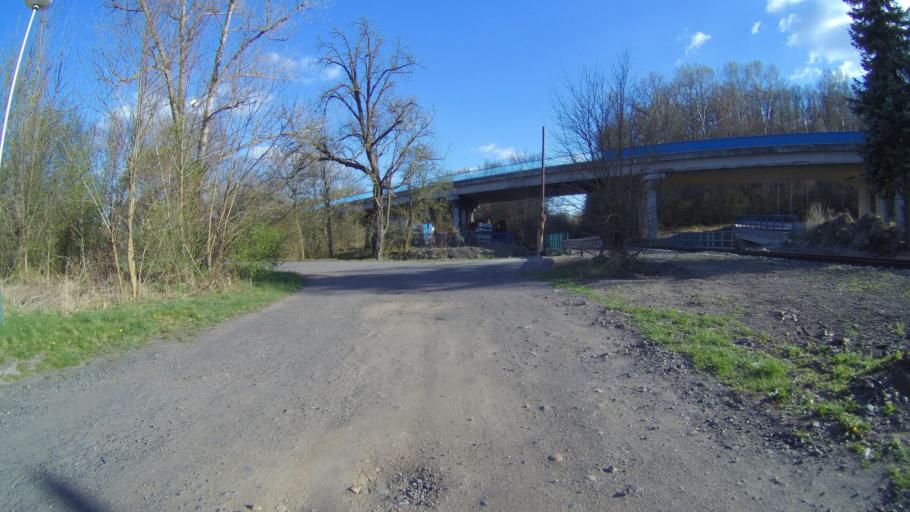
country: CZ
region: Ustecky
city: Zatec
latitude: 50.3170
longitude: 13.5982
